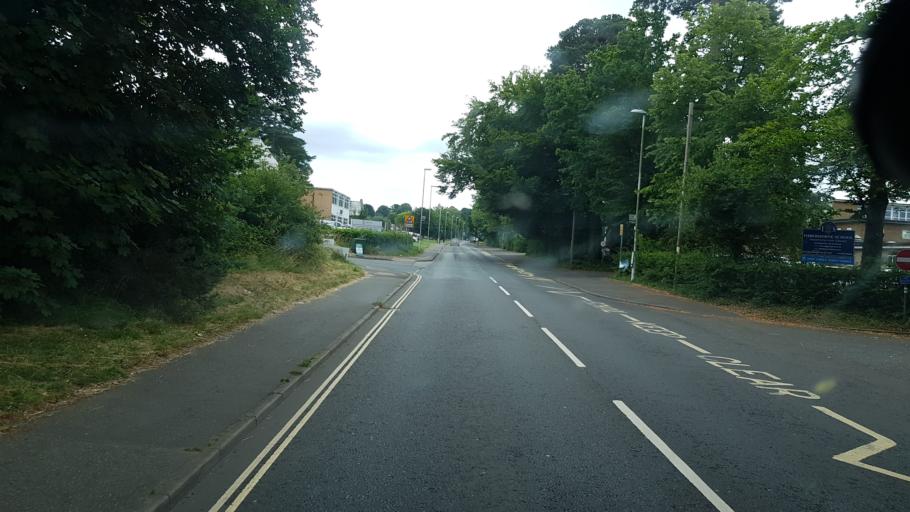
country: GB
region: England
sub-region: Surrey
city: Felbridge
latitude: 51.1352
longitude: -0.0342
